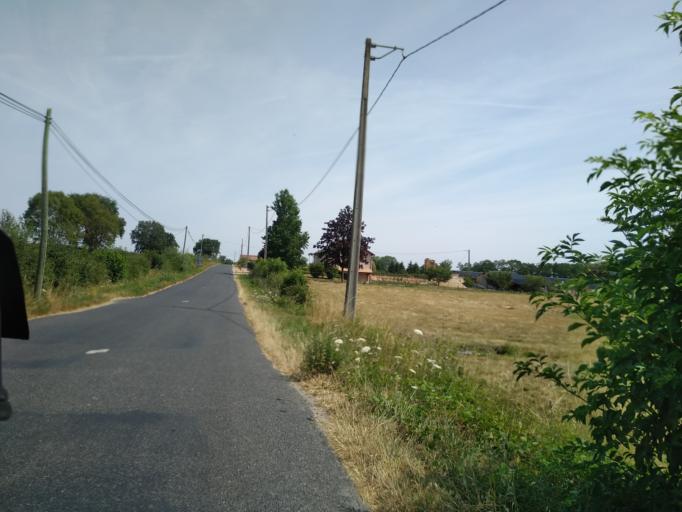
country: FR
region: Auvergne
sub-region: Departement de l'Allier
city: Molinet
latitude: 46.4160
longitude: 3.9754
